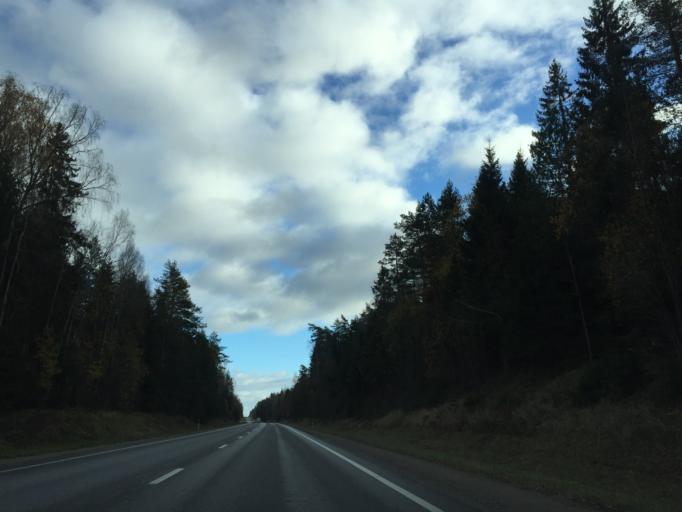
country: LV
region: Tukuma Rajons
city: Tukums
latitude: 57.0008
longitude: 23.0055
